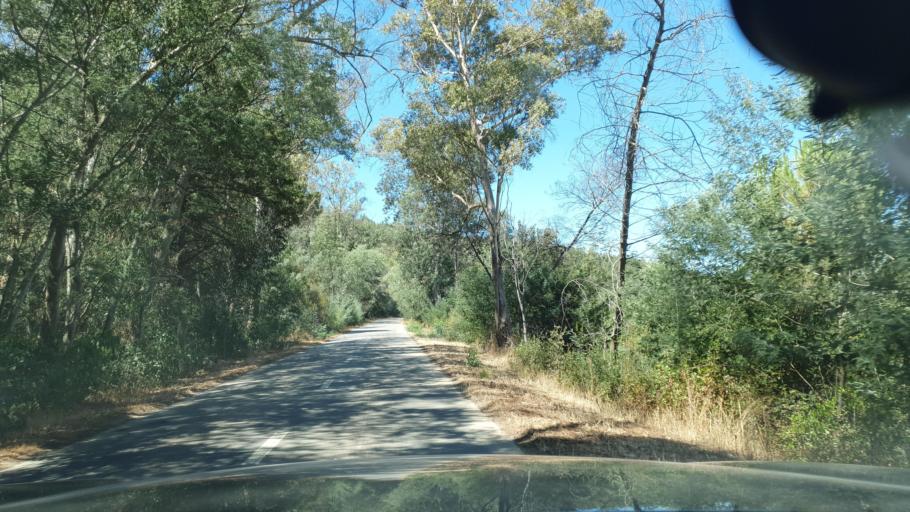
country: PT
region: Beja
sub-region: Odemira
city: Odemira
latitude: 37.5093
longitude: -8.4676
